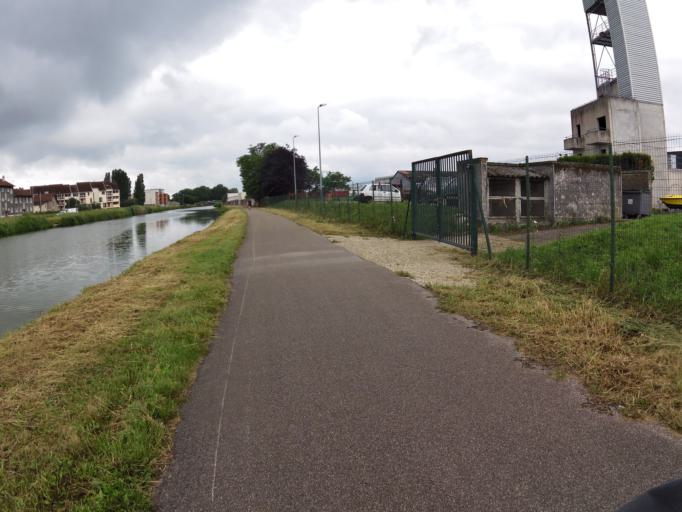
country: FR
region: Champagne-Ardenne
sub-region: Departement de la Haute-Marne
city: Saint-Dizier
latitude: 48.6425
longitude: 4.9421
